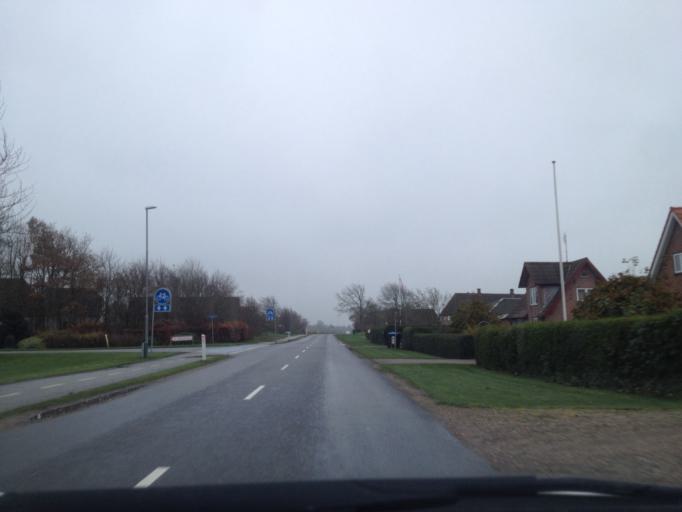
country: DK
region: South Denmark
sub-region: Tonder Kommune
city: Sherrebek
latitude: 55.1199
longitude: 8.7567
